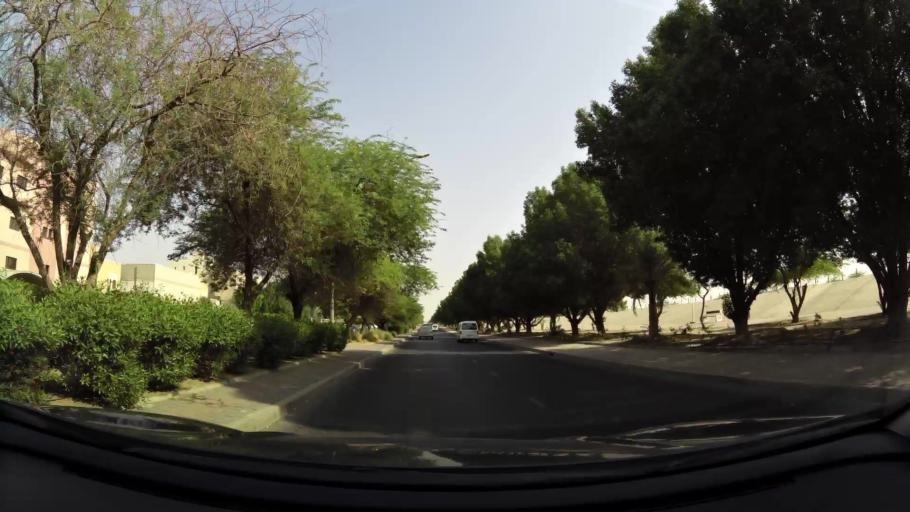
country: KW
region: Muhafazat al Jahra'
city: Al Jahra'
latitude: 29.3181
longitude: 47.6710
